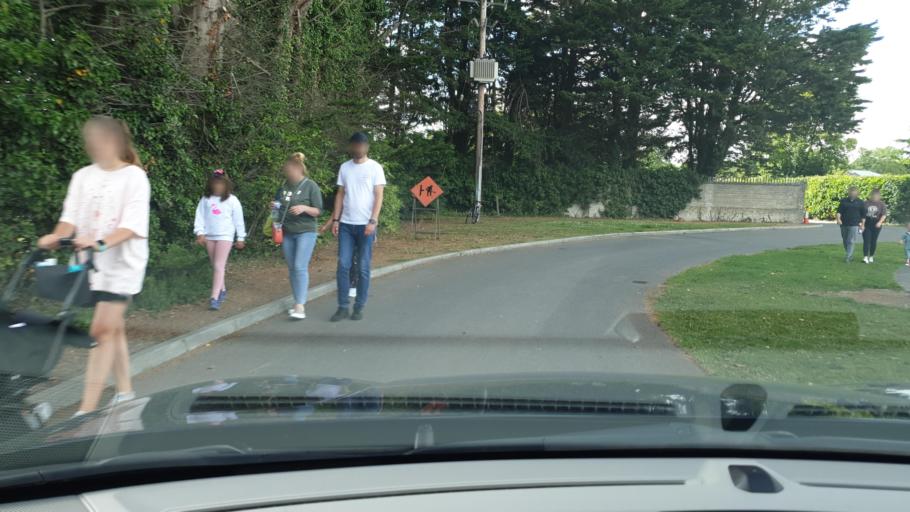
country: IE
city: Confey
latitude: 53.3674
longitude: -6.4705
